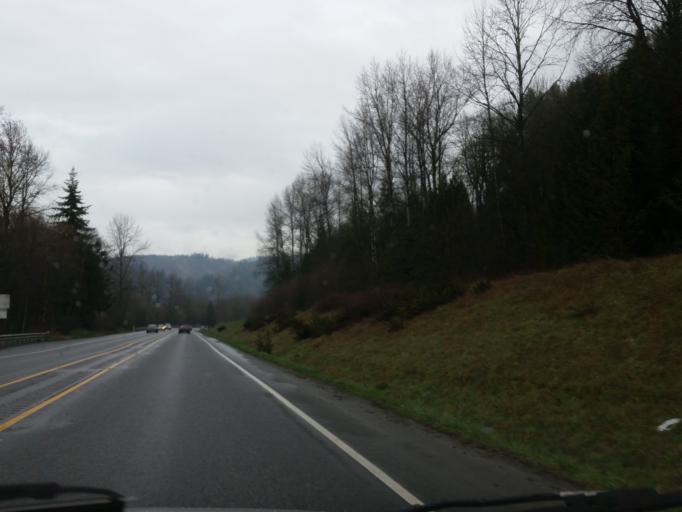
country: US
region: Washington
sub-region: Snohomish County
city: Cathcart
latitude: 47.8260
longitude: -122.0593
